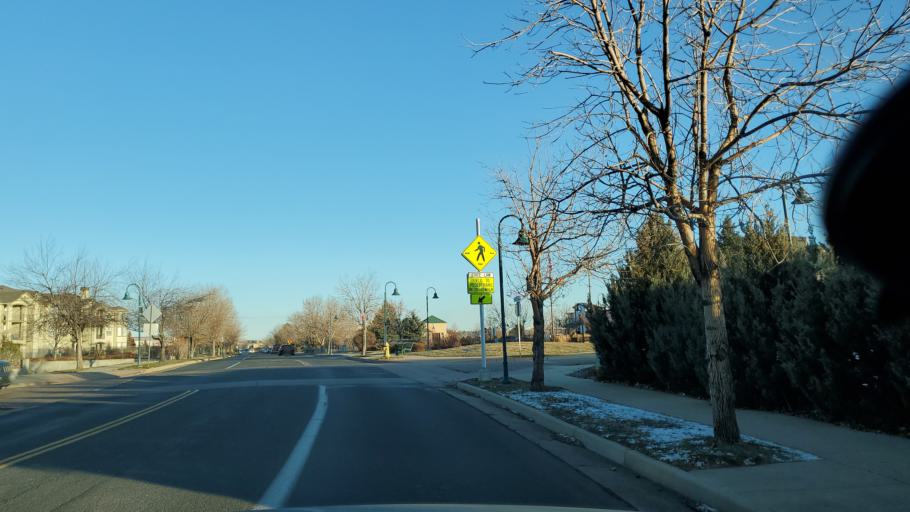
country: US
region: Colorado
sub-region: Broomfield County
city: Broomfield
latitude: 39.9152
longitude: -105.0607
